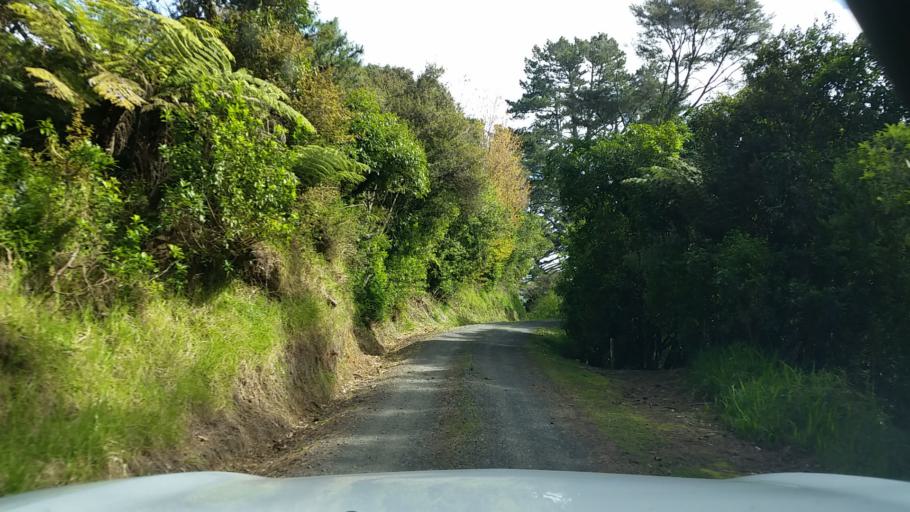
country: NZ
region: Waikato
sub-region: Hauraki District
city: Ngatea
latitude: -37.4624
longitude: 175.4696
